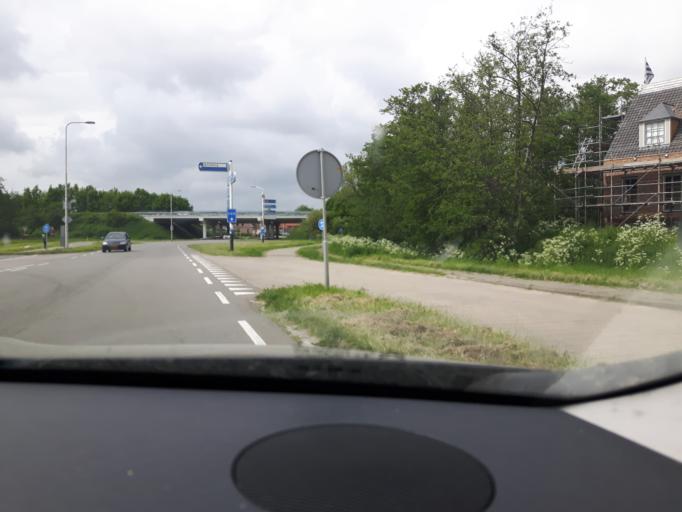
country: NL
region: Zeeland
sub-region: Gemeente Middelburg
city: Middelburg
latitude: 51.4598
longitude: 3.6103
